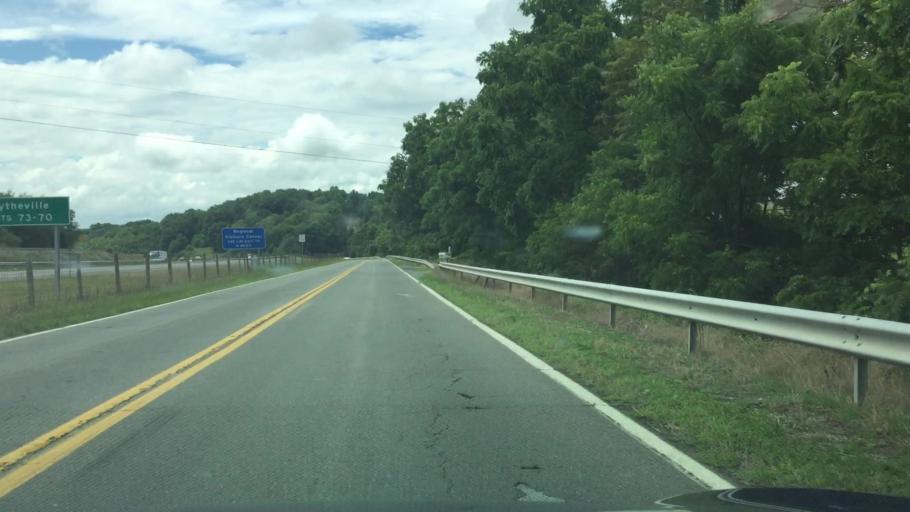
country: US
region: Virginia
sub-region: Wythe County
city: Wytheville
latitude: 36.9396
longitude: -81.0036
